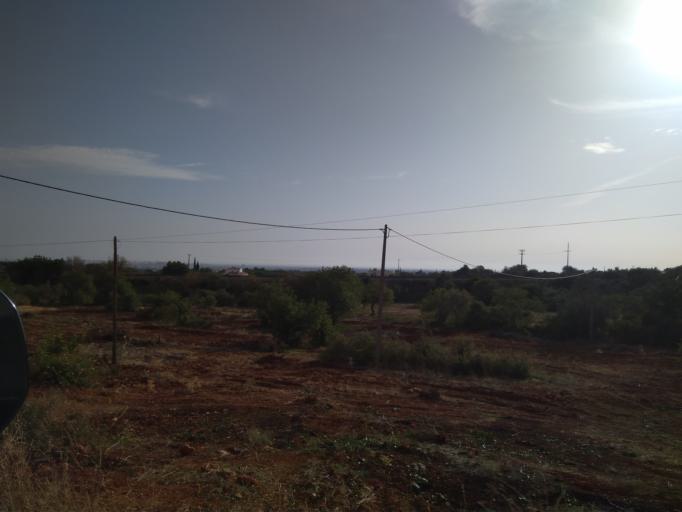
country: PT
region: Faro
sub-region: Faro
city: Santa Barbara de Nexe
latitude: 37.0978
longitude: -7.9557
